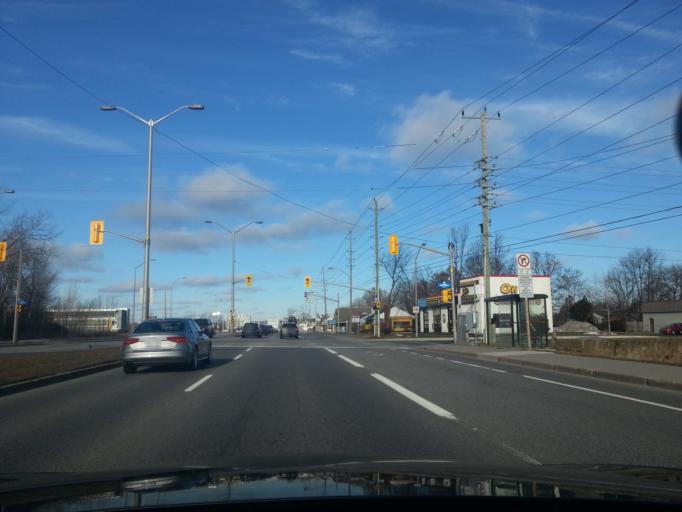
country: CA
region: Ontario
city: Bells Corners
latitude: 45.3387
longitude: -75.7546
